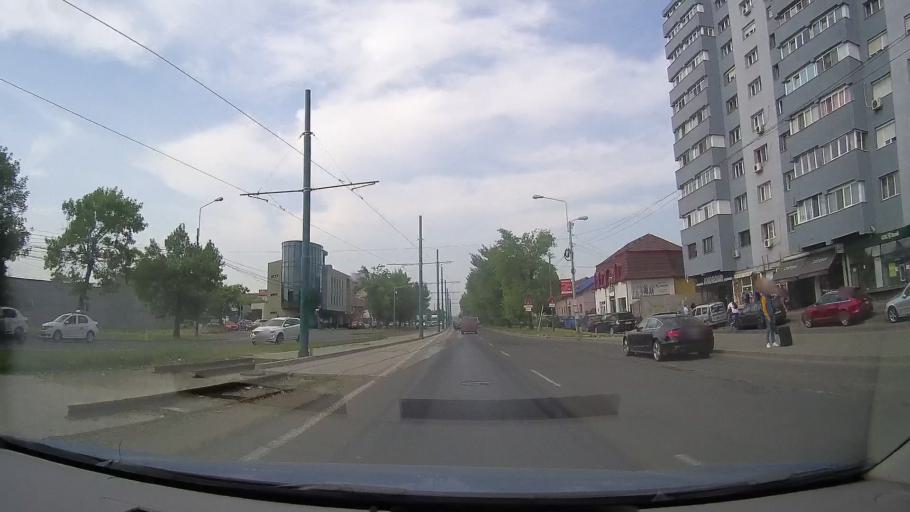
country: RO
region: Timis
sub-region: Comuna Giroc
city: Chisoda
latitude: 45.7280
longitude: 21.2045
